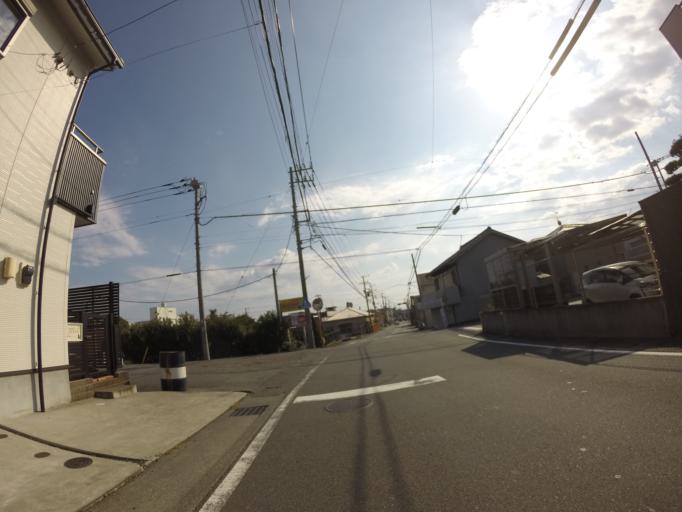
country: JP
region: Shizuoka
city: Fujinomiya
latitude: 35.1883
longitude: 138.6460
